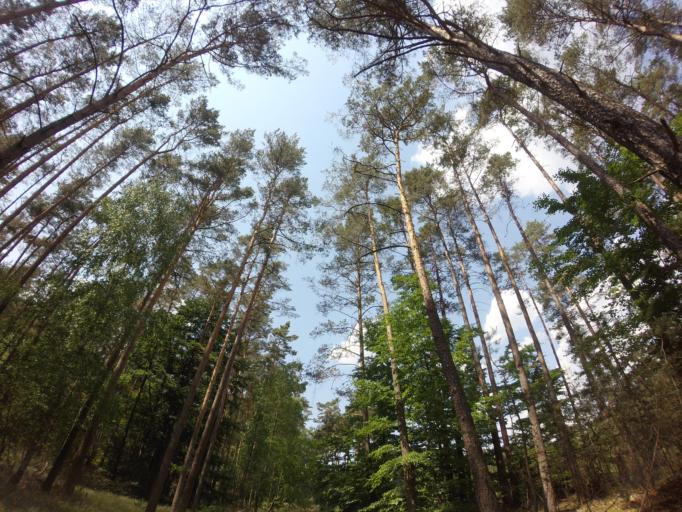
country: PL
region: West Pomeranian Voivodeship
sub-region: Powiat choszczenski
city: Bierzwnik
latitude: 53.0845
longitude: 15.6950
